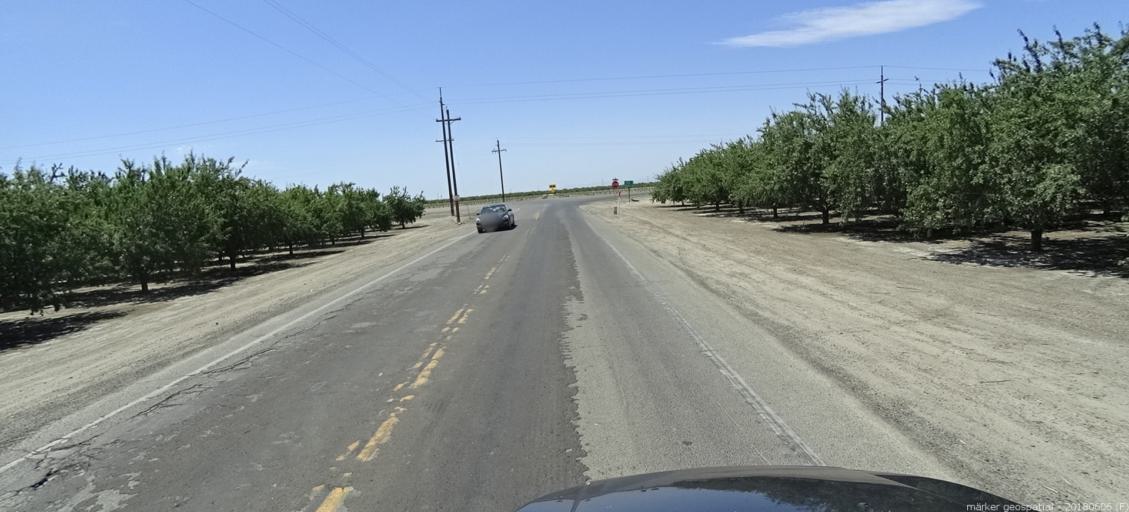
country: US
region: California
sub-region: Fresno County
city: Firebaugh
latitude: 36.8595
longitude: -120.3819
